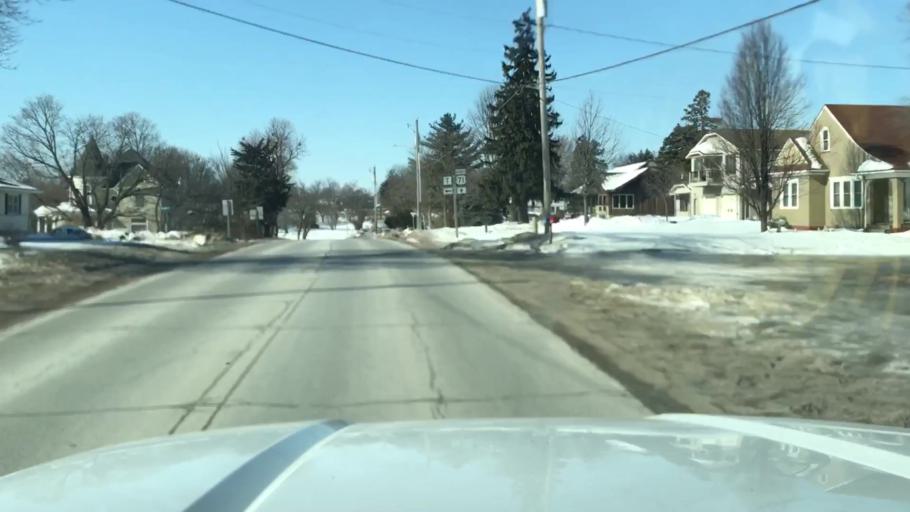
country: US
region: Missouri
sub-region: Andrew County
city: Savannah
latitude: 39.9467
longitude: -94.8308
